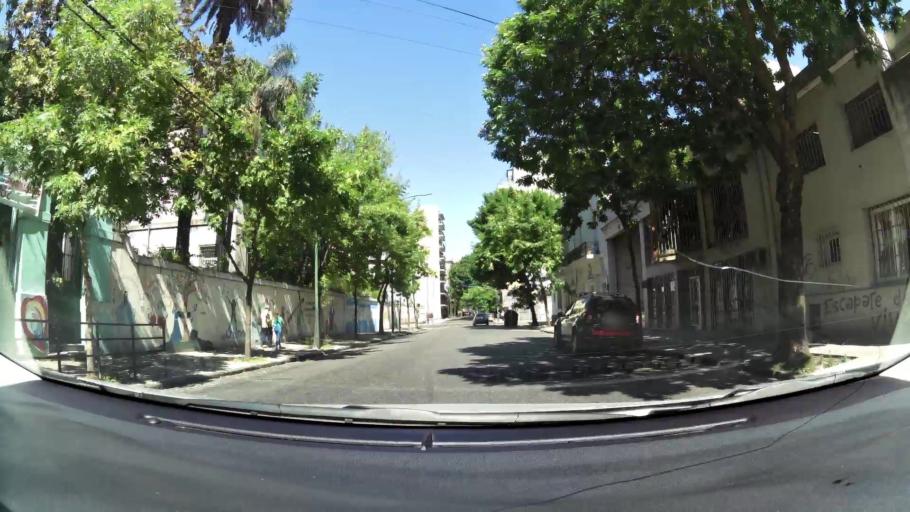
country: AR
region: Buenos Aires F.D.
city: Buenos Aires
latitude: -34.6250
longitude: -58.3891
